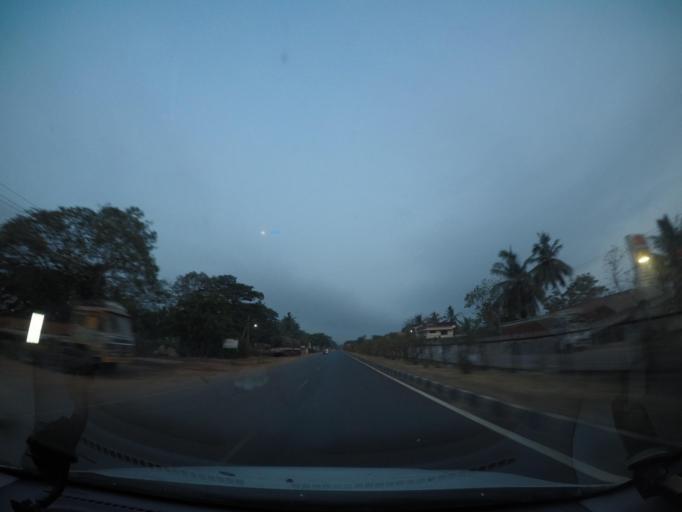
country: IN
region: Andhra Pradesh
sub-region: West Godavari
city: Tadepallegudem
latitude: 16.8201
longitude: 81.4025
